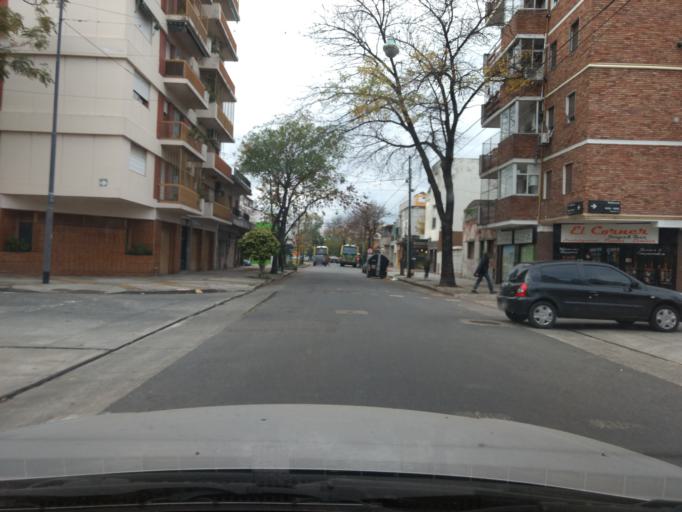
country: AR
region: Buenos Aires F.D.
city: Villa Santa Rita
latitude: -34.6115
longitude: -58.5086
